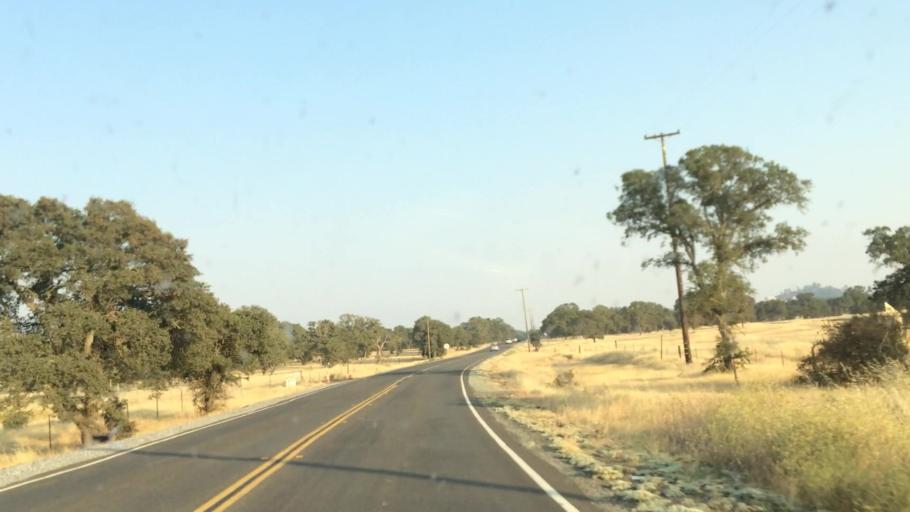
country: US
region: California
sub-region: Amador County
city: Ione
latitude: 38.3925
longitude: -120.9973
